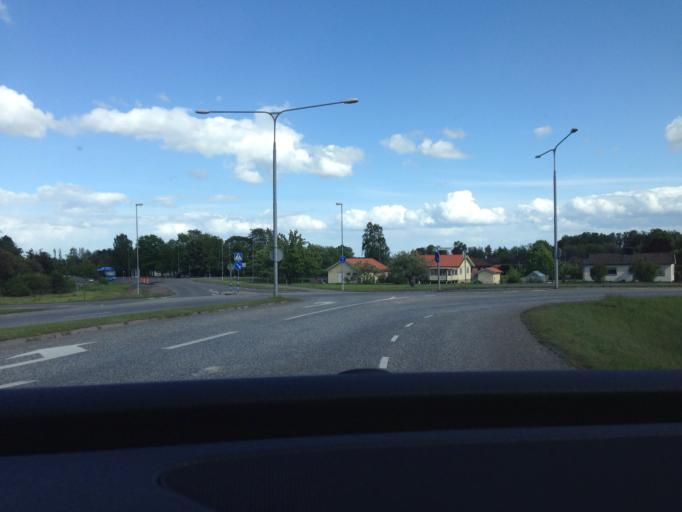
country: SE
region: Vaestra Goetaland
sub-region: Skovde Kommun
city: Skoevde
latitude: 58.4136
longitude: 13.8672
